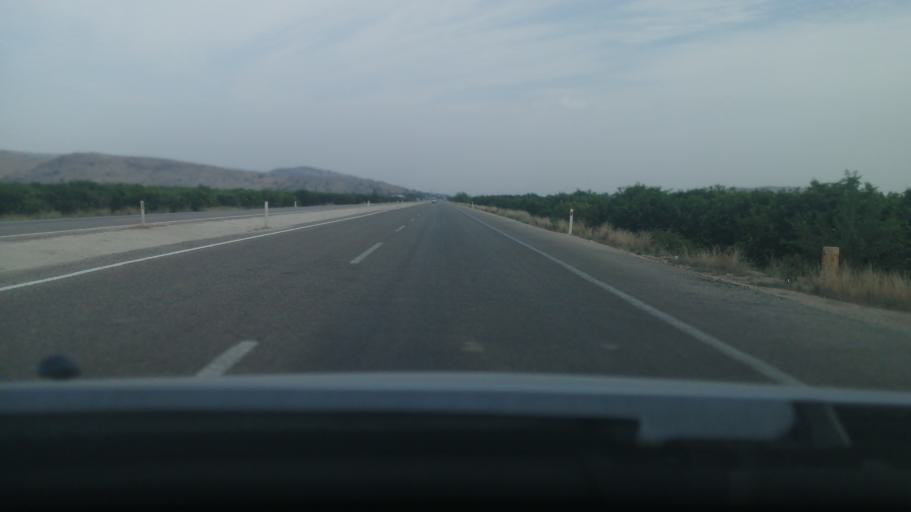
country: TR
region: Adana
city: Kozan
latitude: 37.3848
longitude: 35.8086
